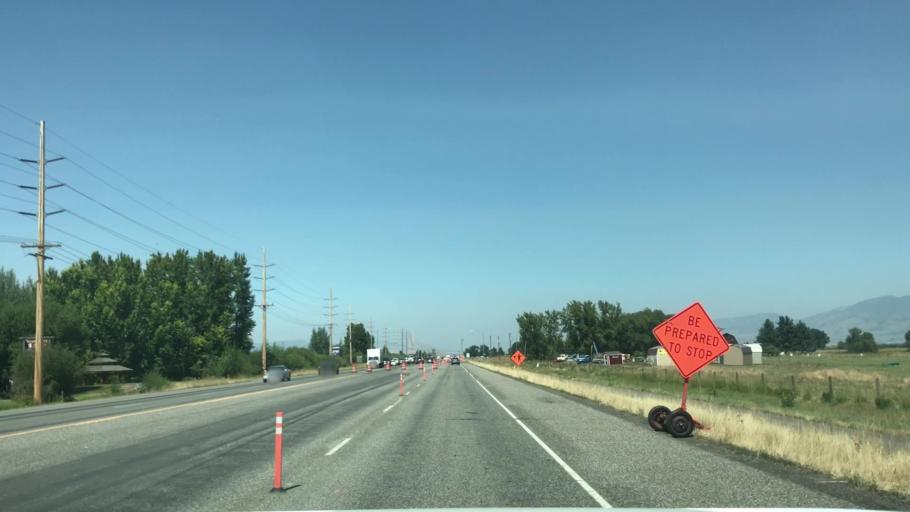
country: US
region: Montana
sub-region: Gallatin County
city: Belgrade
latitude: 45.7120
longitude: -111.1851
